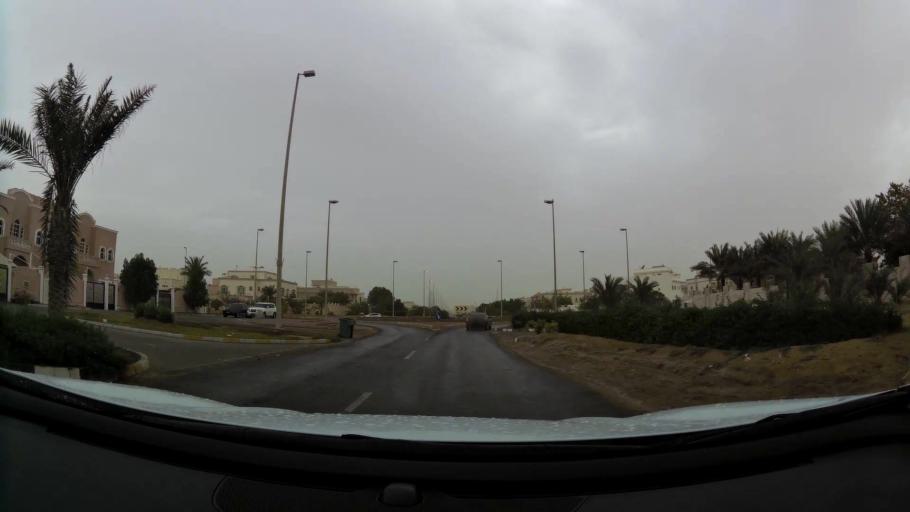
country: AE
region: Abu Dhabi
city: Abu Dhabi
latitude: 24.4230
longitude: 54.5827
